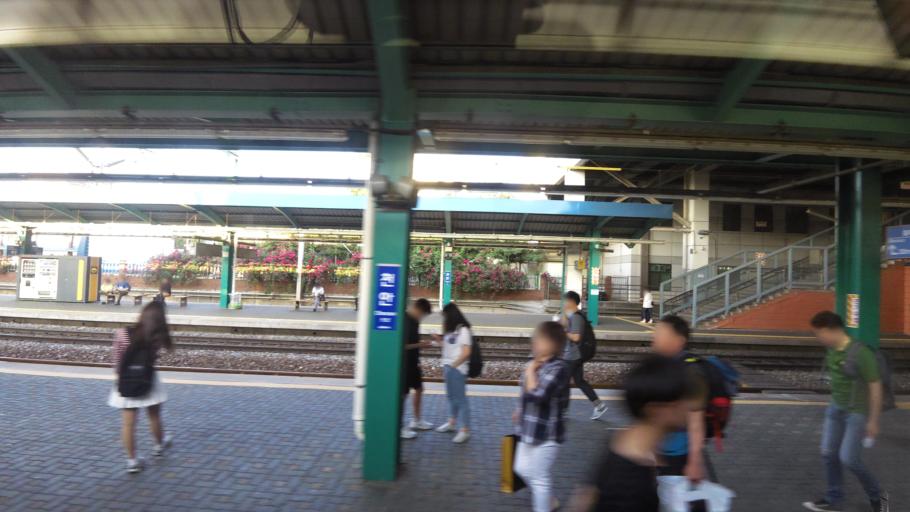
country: KR
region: Chungcheongnam-do
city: Cheonan
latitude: 36.8092
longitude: 127.1468
